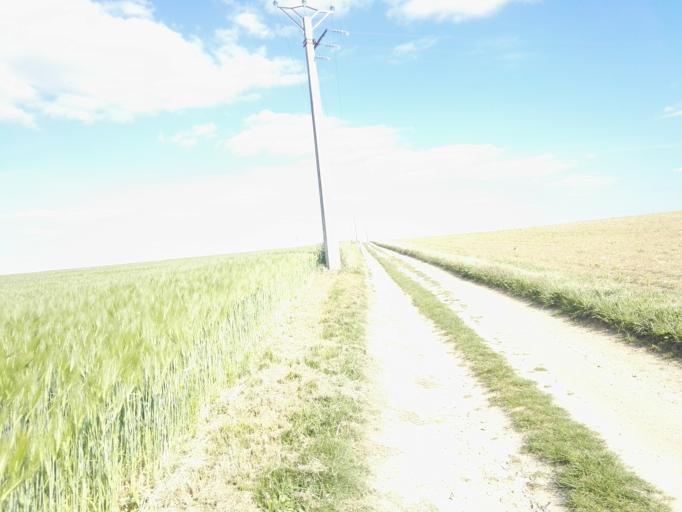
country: FR
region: Haute-Normandie
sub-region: Departement de l'Eure
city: Pacy-sur-Eure
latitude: 48.9900
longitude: 1.3707
